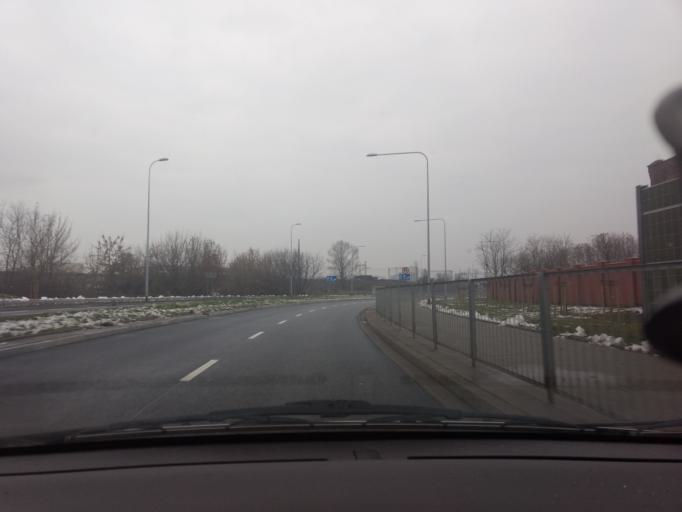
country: PL
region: Masovian Voivodeship
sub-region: Warszawa
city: Praga Poludnie
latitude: 52.2579
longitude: 21.0638
